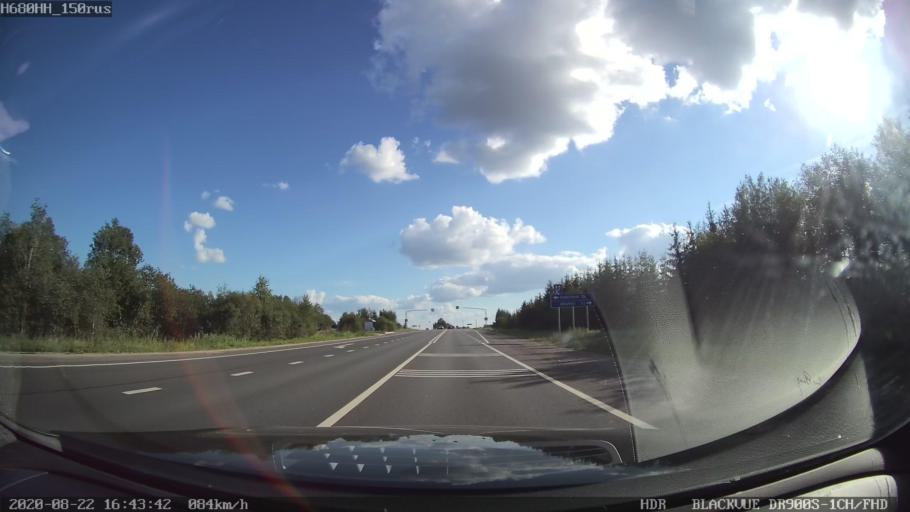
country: RU
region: Tverskaya
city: Rameshki
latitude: 57.3176
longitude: 36.0891
